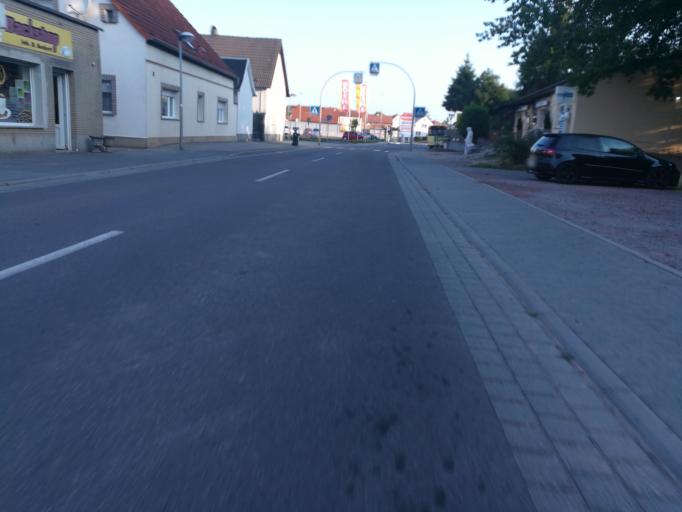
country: DE
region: Saxony-Anhalt
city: Irxleben
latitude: 52.1648
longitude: 11.4834
